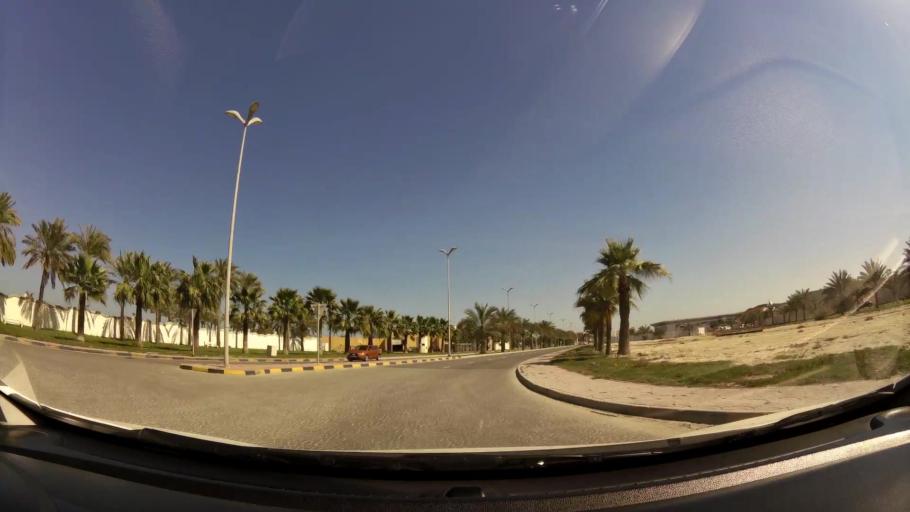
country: BH
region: Muharraq
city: Al Hadd
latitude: 26.2798
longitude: 50.6605
